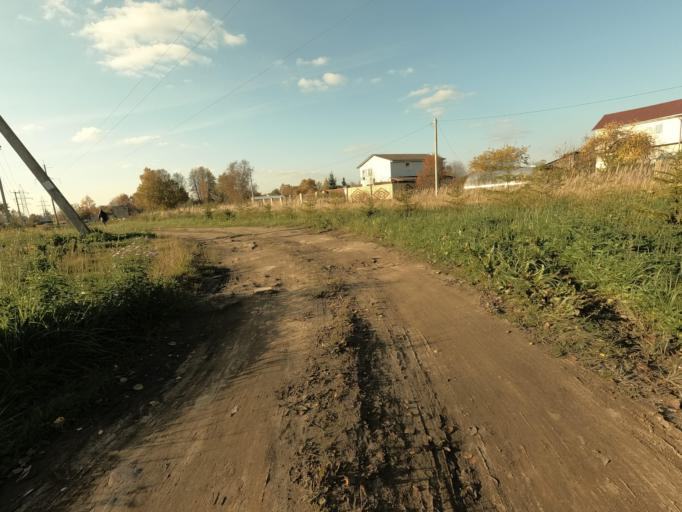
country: RU
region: Leningrad
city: Mga
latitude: 59.7507
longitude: 31.0587
